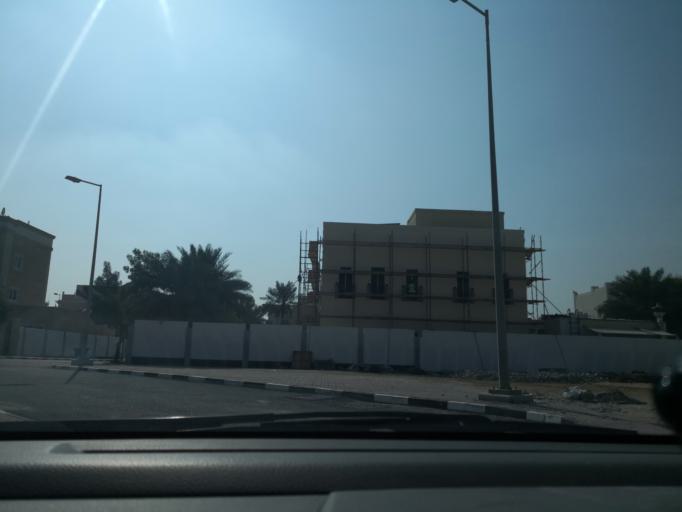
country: QA
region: Baladiyat ad Dawhah
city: Doha
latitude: 25.3269
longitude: 51.5108
